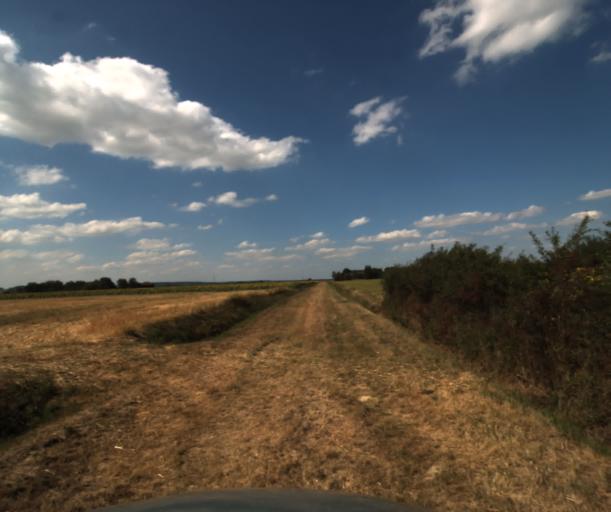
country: FR
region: Midi-Pyrenees
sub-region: Departement de la Haute-Garonne
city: Saint-Lys
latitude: 43.5262
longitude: 1.1787
